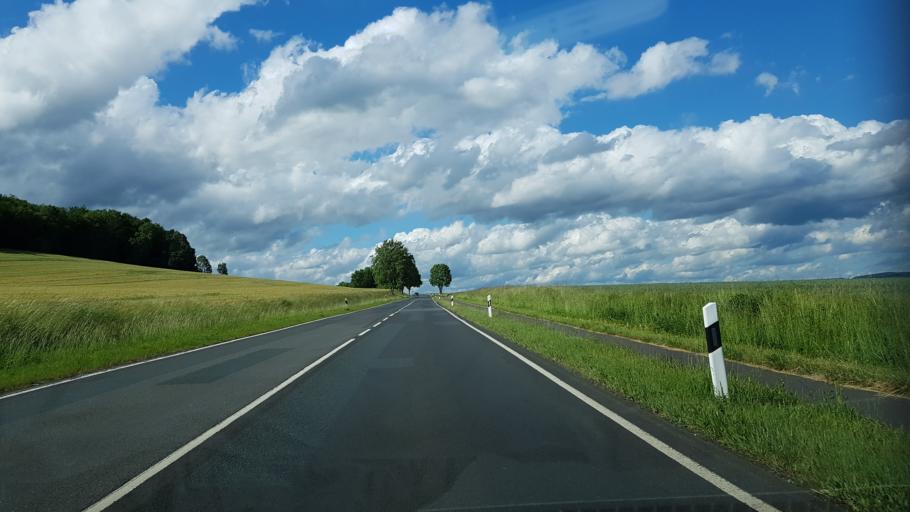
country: DE
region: Lower Saxony
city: Hardegsen
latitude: 51.6043
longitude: 9.8536
